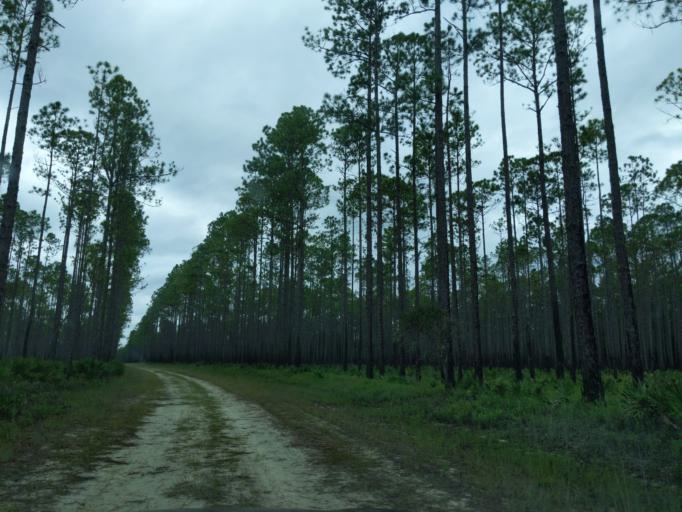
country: US
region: Florida
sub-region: Gadsden County
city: Midway
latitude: 30.3770
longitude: -84.4878
